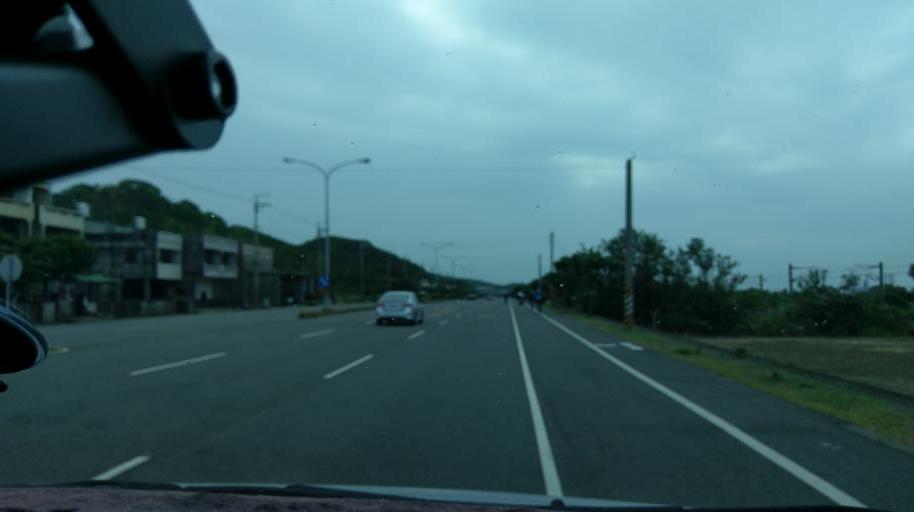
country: TW
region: Taiwan
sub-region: Miaoli
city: Miaoli
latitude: 24.5241
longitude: 120.6923
